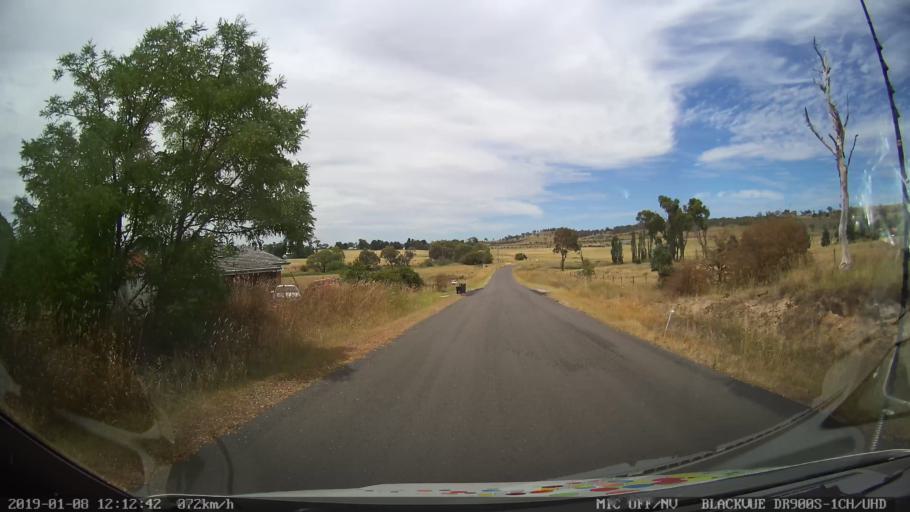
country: AU
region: New South Wales
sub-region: Armidale Dumaresq
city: Armidale
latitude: -30.4593
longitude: 151.6085
